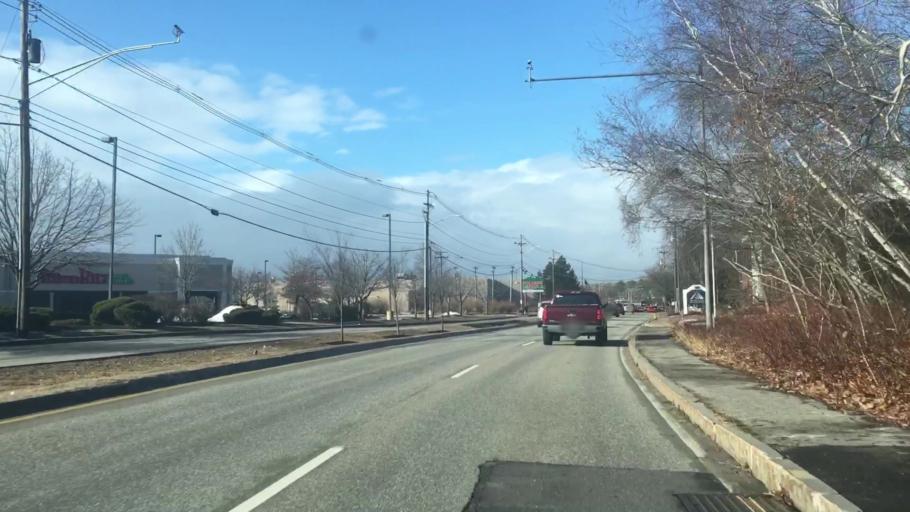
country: US
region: Maine
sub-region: Cumberland County
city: South Portland Gardens
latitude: 43.6340
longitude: -70.3255
